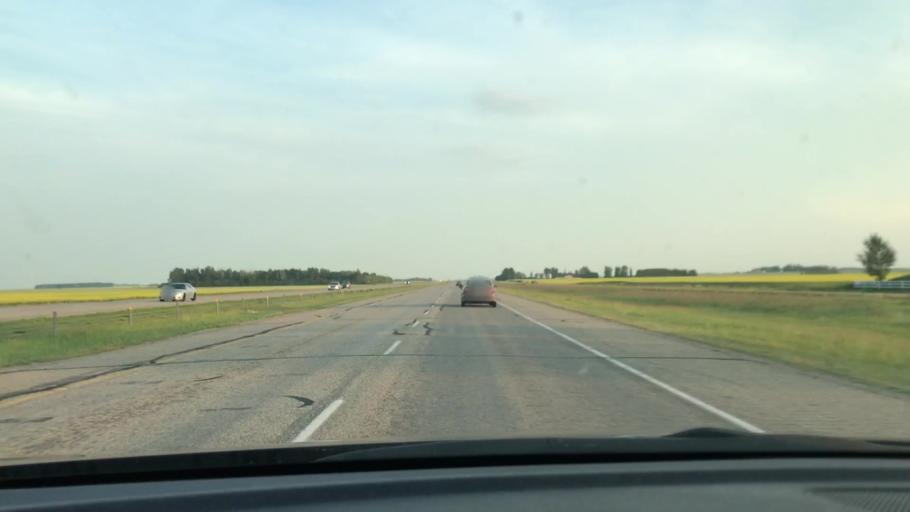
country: CA
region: Alberta
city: Olds
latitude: 51.8424
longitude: -114.0256
